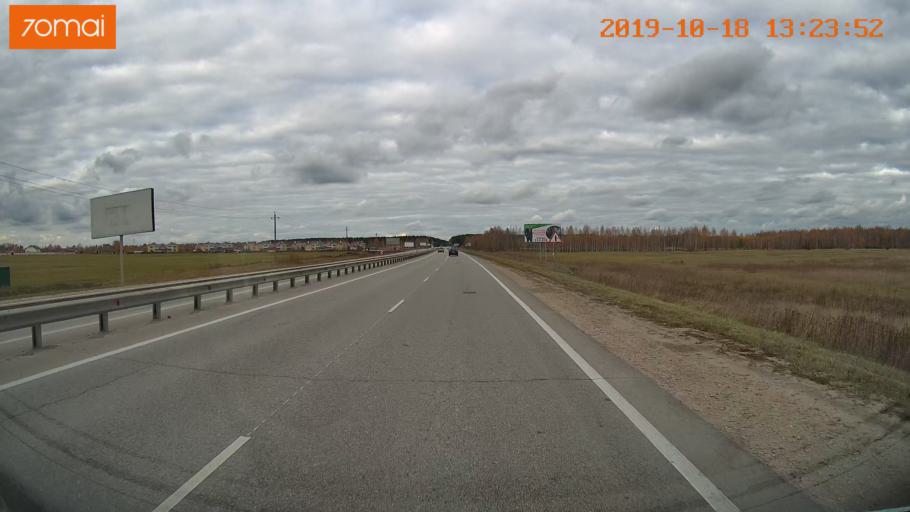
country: RU
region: Rjazan
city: Polyany
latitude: 54.7226
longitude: 39.8471
